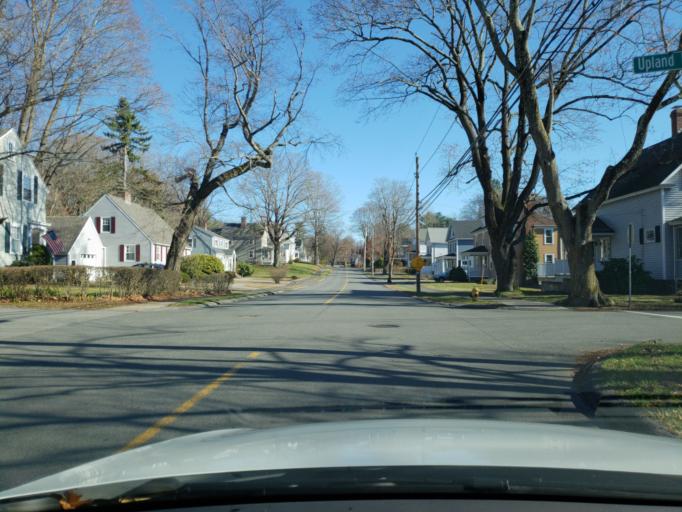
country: US
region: Massachusetts
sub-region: Essex County
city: Andover
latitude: 42.6591
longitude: -71.1302
